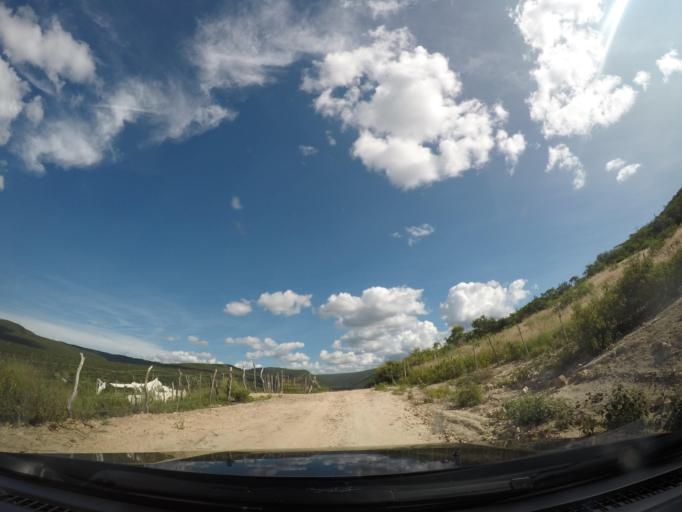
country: BR
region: Bahia
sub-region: Barra Da Estiva
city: Barra da Estiva
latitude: -13.2099
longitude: -41.5913
